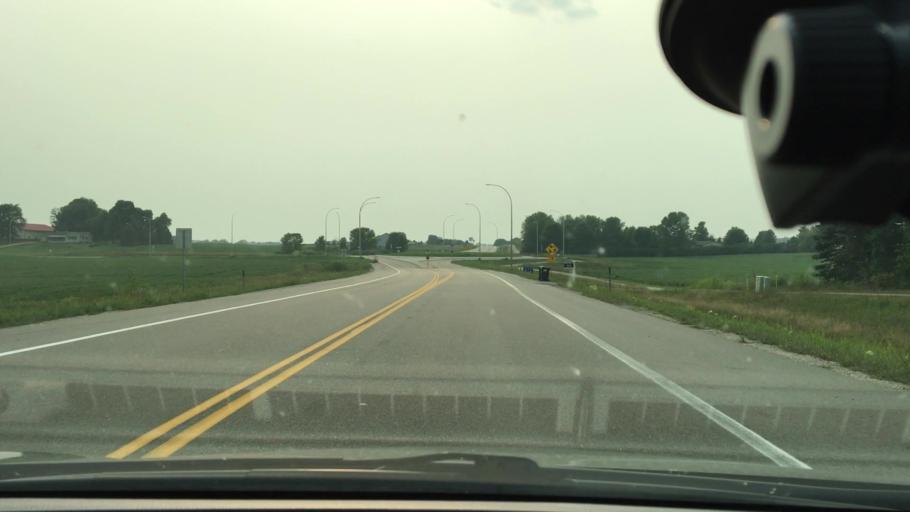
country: US
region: Minnesota
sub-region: Wright County
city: Otsego
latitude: 45.2524
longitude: -93.5978
